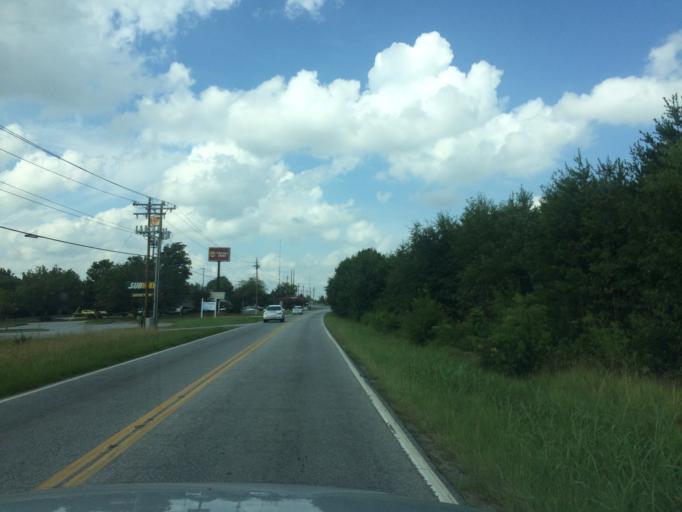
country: US
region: South Carolina
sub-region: Spartanburg County
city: Fairforest
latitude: 34.9653
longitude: -82.0012
